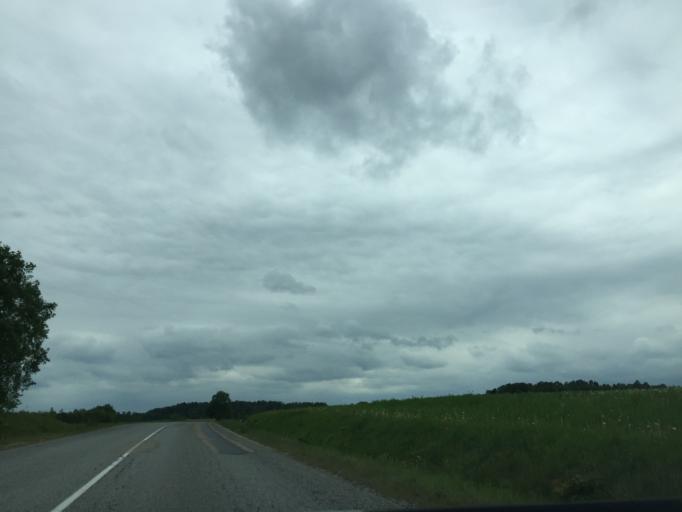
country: LV
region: Aglona
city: Aglona
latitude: 56.1319
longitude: 27.0704
